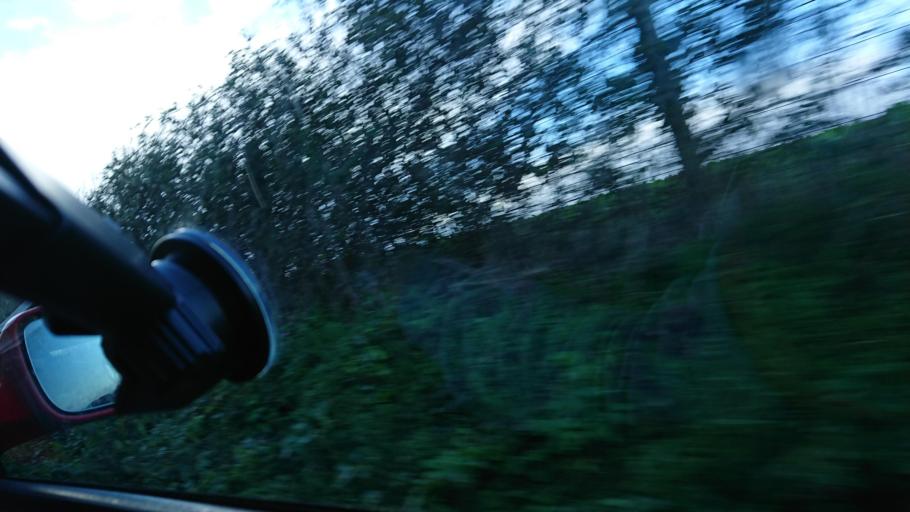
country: GB
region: England
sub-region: Cornwall
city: Looe
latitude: 50.3416
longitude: -4.4808
